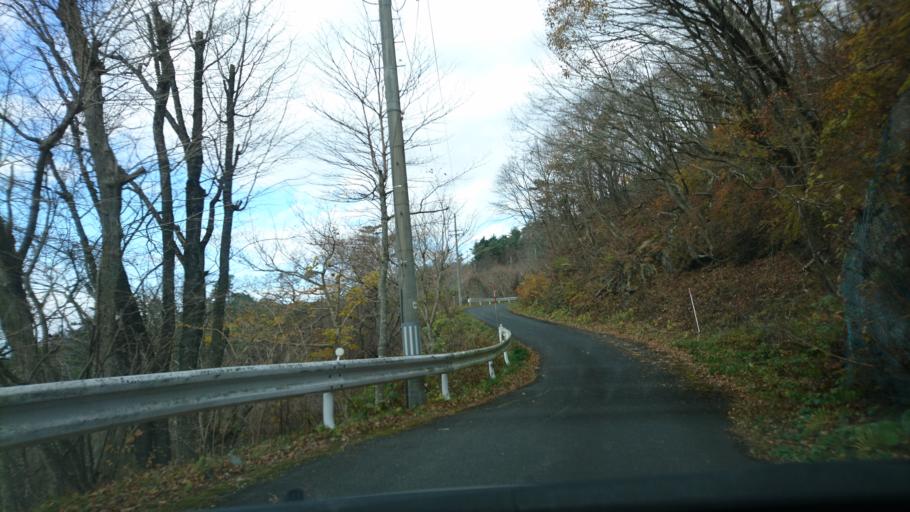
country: JP
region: Iwate
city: Ichinoseki
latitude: 39.0125
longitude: 141.1813
